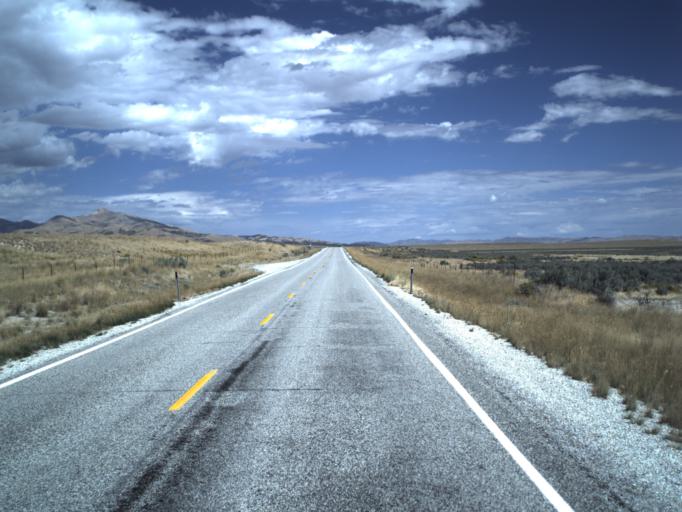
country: US
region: Idaho
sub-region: Oneida County
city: Malad City
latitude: 41.9333
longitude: -113.0882
